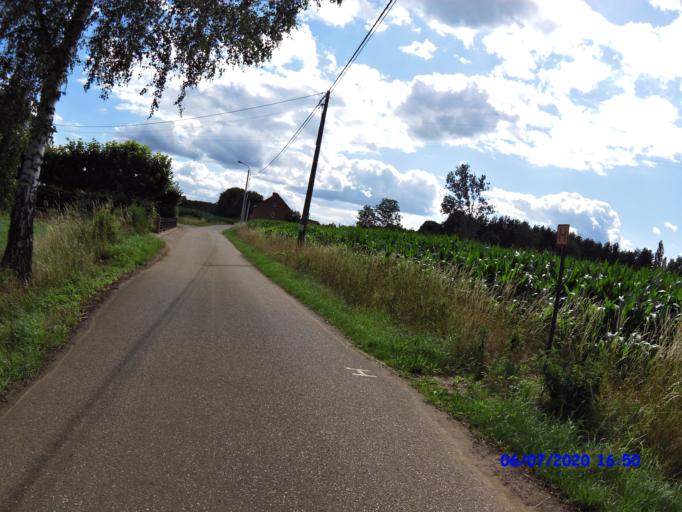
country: BE
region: Flanders
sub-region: Provincie Antwerpen
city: Meerhout
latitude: 51.1300
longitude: 5.1184
